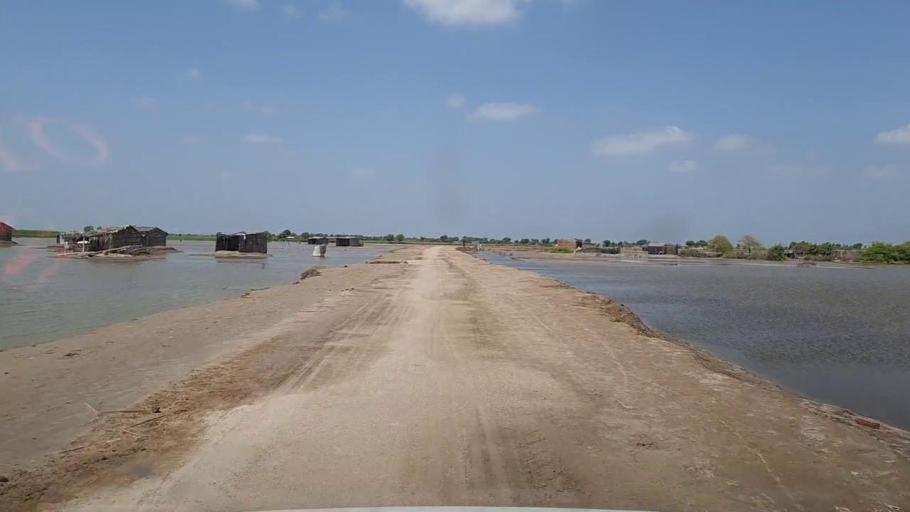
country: PK
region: Sindh
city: Kario
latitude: 24.6948
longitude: 68.5870
